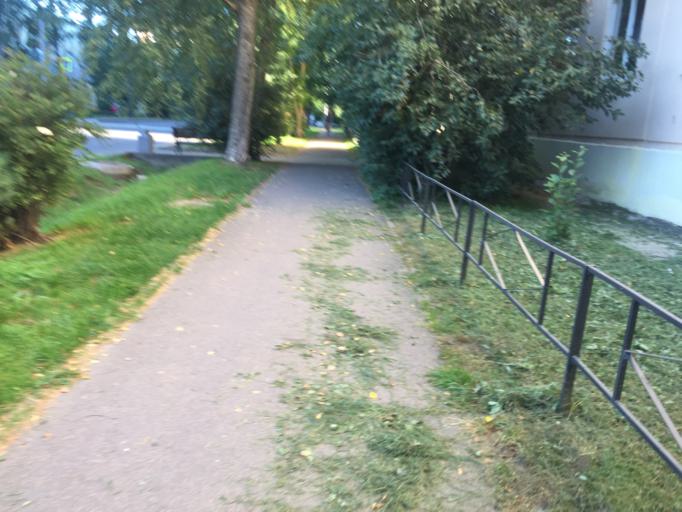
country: RU
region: Leningrad
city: Murino
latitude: 60.0384
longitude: 30.4653
